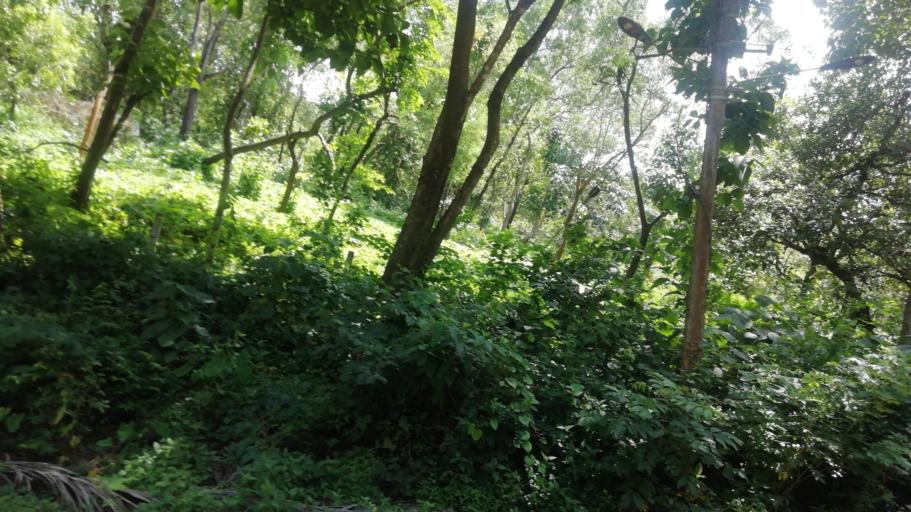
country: IN
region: Goa
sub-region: North Goa
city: Ponda
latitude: 15.3902
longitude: 74.0058
